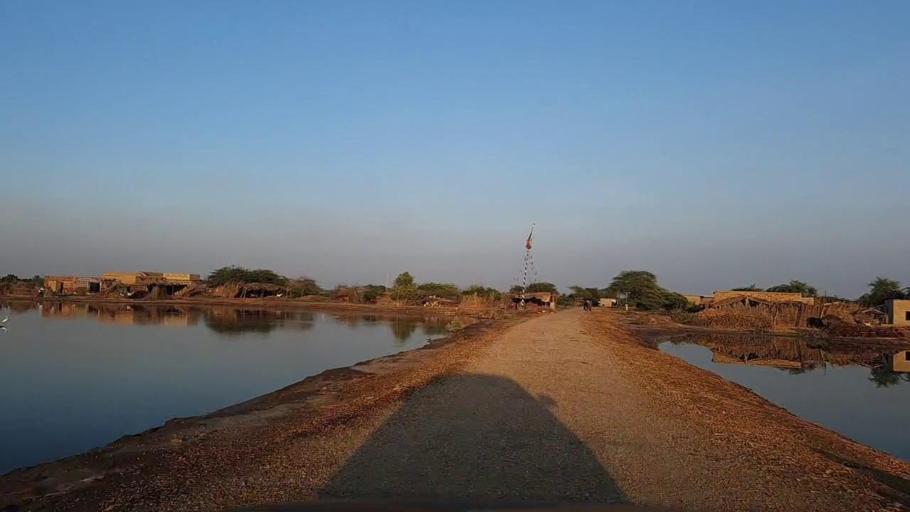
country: PK
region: Sindh
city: Thatta
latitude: 24.6643
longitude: 67.9180
